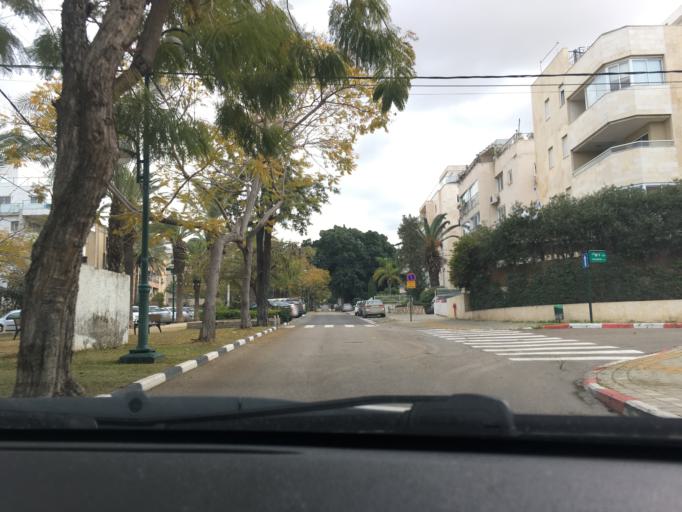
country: IL
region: Tel Aviv
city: Ramat HaSharon
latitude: 32.1453
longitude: 34.8405
